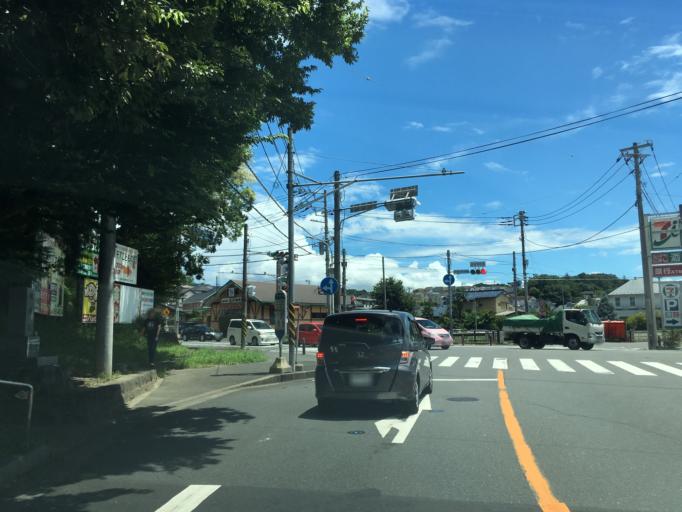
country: JP
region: Tokyo
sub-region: Machida-shi
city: Machida
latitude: 35.5544
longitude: 139.4895
